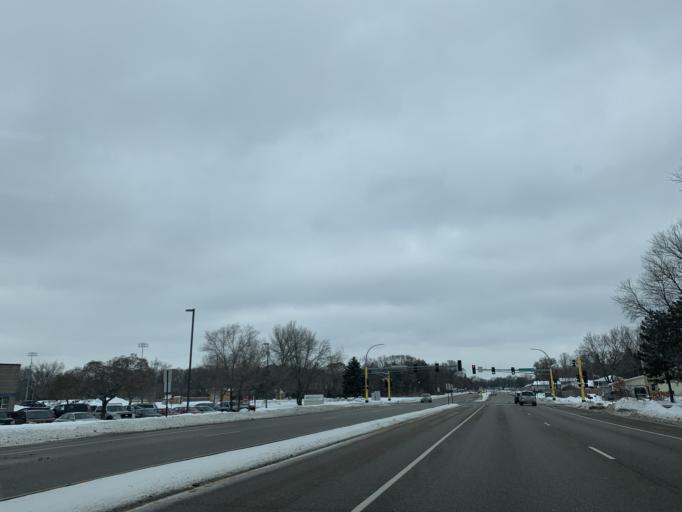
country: US
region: Minnesota
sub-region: Anoka County
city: Blaine
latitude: 45.1562
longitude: -93.2733
